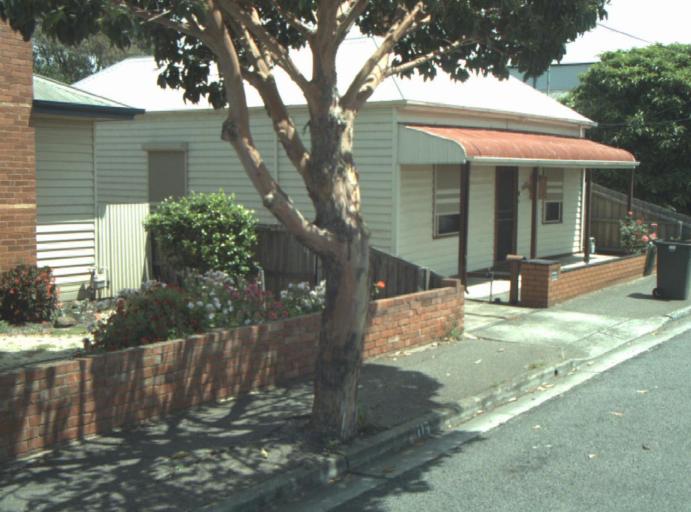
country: AU
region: Victoria
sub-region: Greater Geelong
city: Geelong West
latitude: -38.1387
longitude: 144.3384
